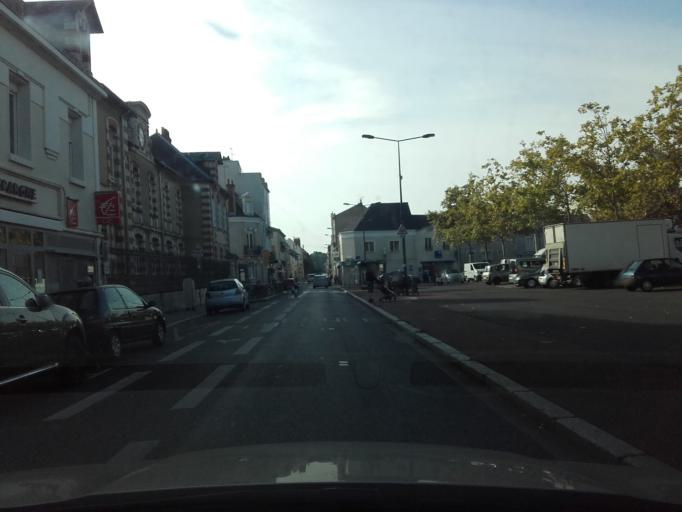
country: FR
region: Centre
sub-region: Departement d'Indre-et-Loire
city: Tours
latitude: 47.3875
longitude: 0.7031
